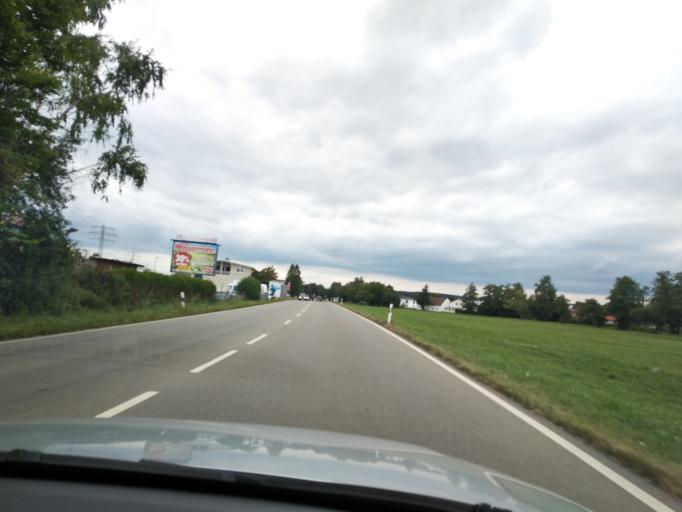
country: DE
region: Bavaria
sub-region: Swabia
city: Memmingen
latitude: 47.9860
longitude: 10.2027
